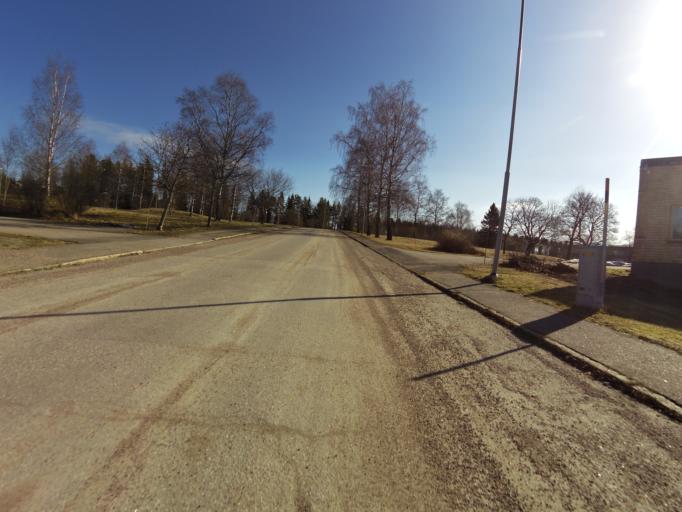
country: SE
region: Gaevleborg
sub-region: Hofors Kommun
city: Hofors
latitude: 60.5510
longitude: 16.2695
